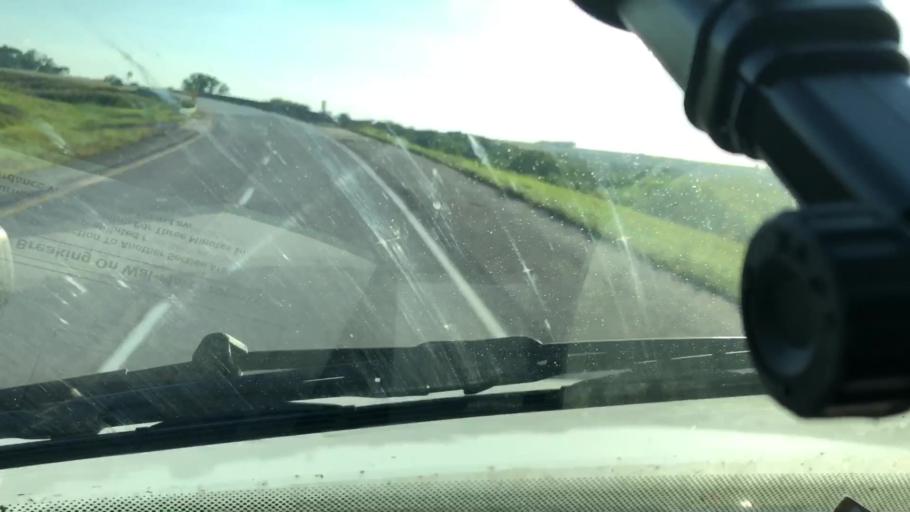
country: US
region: Iowa
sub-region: Pottawattamie County
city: Avoca
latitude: 41.4979
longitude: -95.5827
